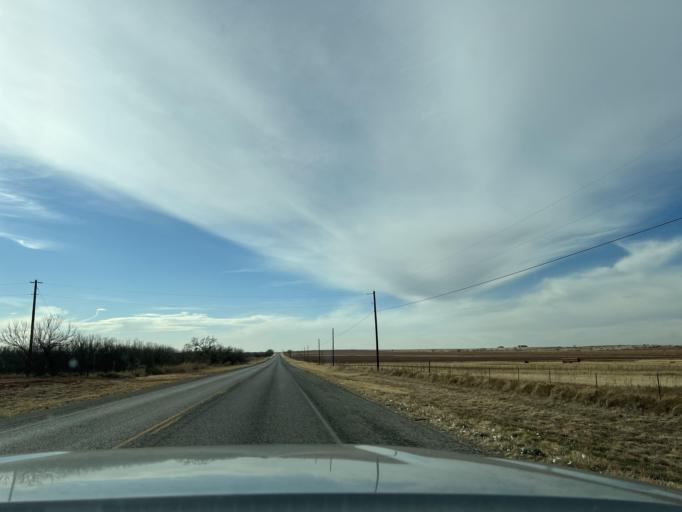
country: US
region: Texas
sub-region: Fisher County
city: Roby
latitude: 32.7411
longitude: -100.4708
